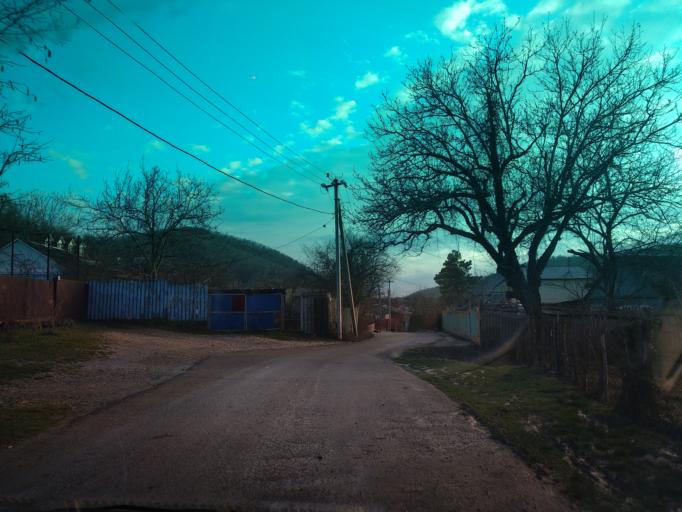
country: RU
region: Krasnodarskiy
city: Novomikhaylovskiy
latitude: 44.2745
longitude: 38.8346
